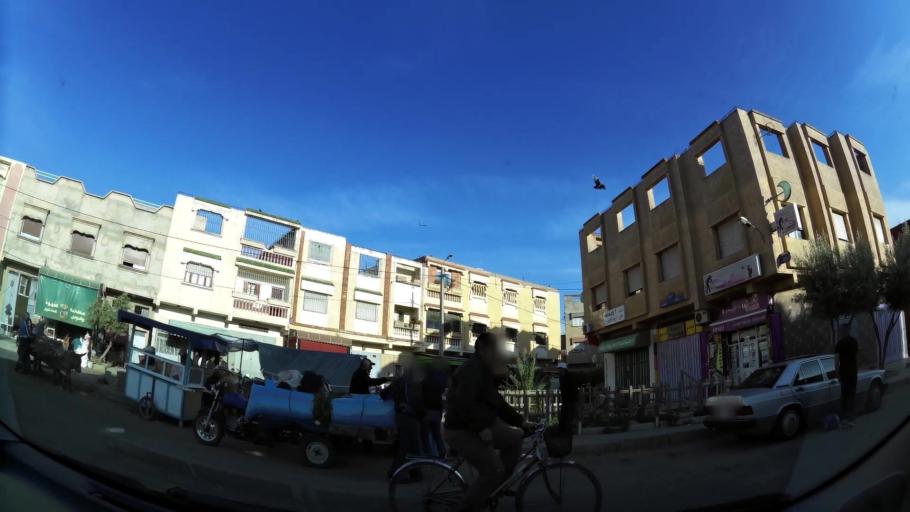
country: MA
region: Oriental
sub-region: Oujda-Angad
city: Oujda
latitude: 34.7080
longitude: -1.8971
